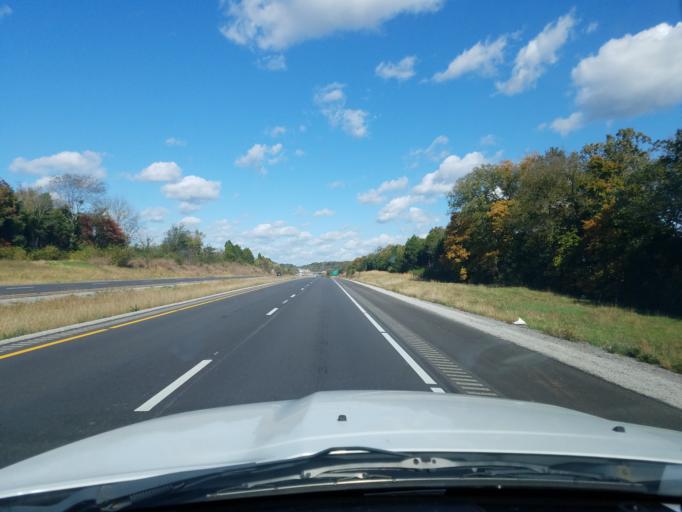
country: US
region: Kentucky
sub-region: Warren County
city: Bowling Green
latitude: 36.9814
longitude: -86.5015
